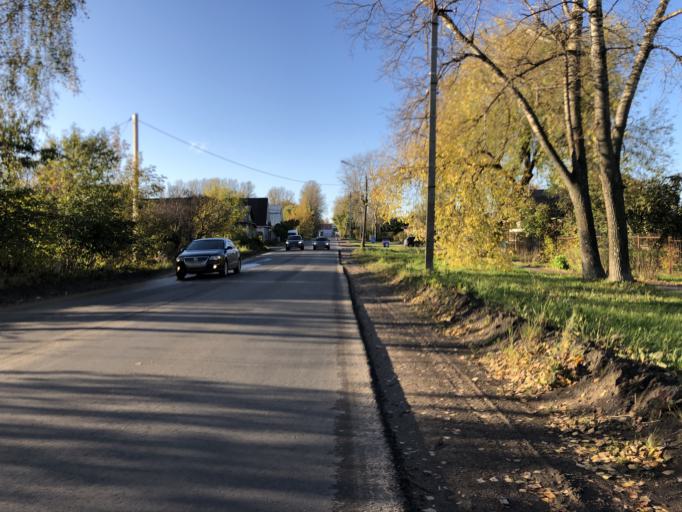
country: RU
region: Tverskaya
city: Rzhev
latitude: 56.2440
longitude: 34.3426
